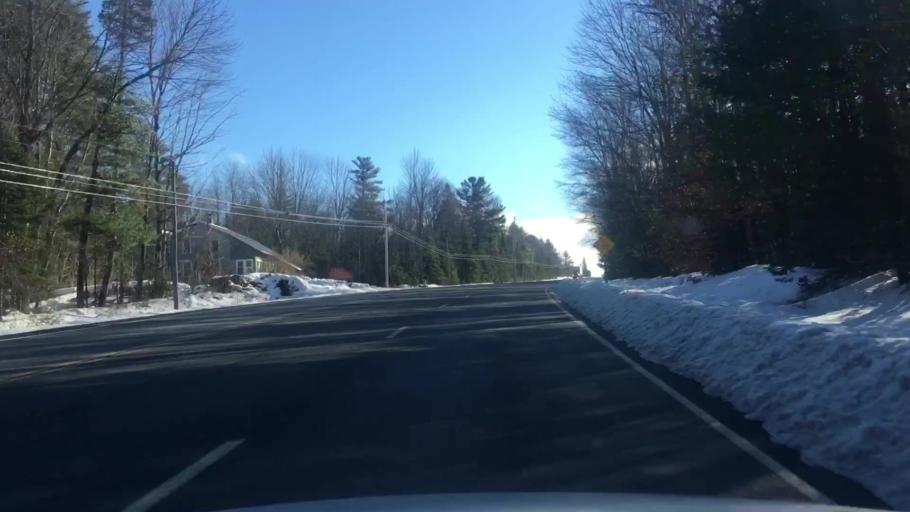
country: US
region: Maine
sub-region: Somerset County
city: Madison
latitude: 44.8990
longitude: -69.8105
